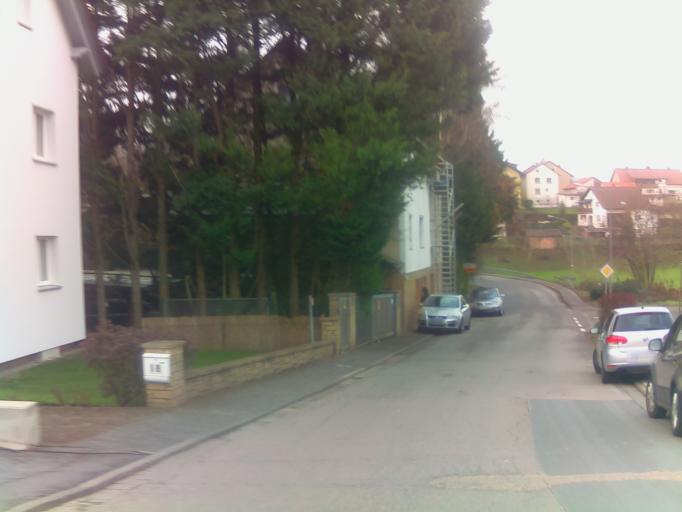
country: DE
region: Hesse
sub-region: Regierungsbezirk Darmstadt
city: Furth
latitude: 49.6620
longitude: 8.8002
